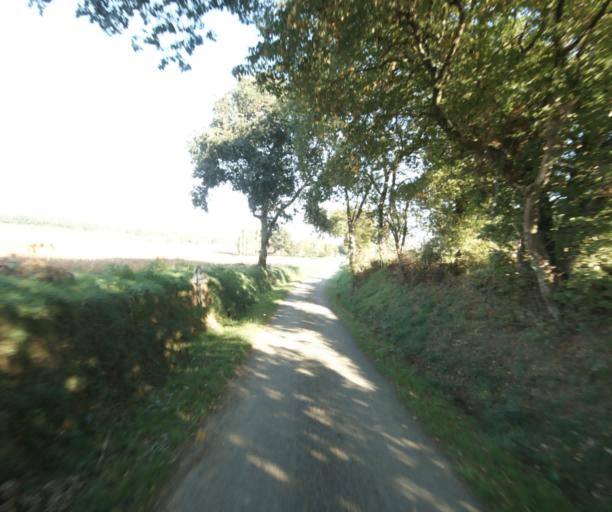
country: FR
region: Midi-Pyrenees
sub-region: Departement du Gers
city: Eauze
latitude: 43.7967
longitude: 0.1272
